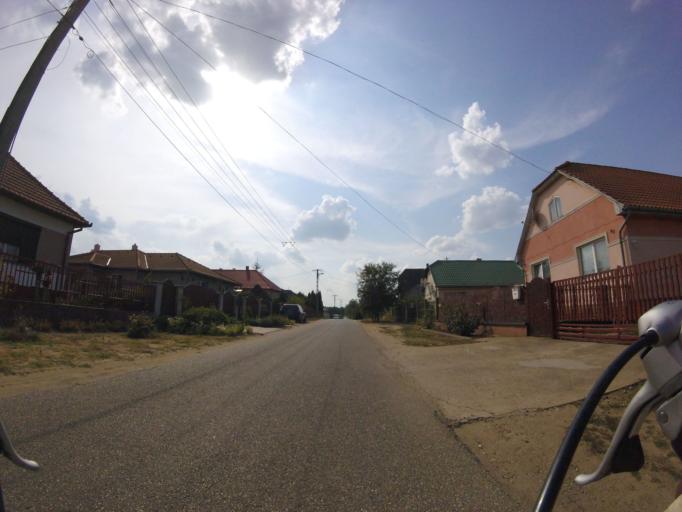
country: HU
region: Szabolcs-Szatmar-Bereg
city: Nyirpazony
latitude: 48.0140
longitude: 21.8211
